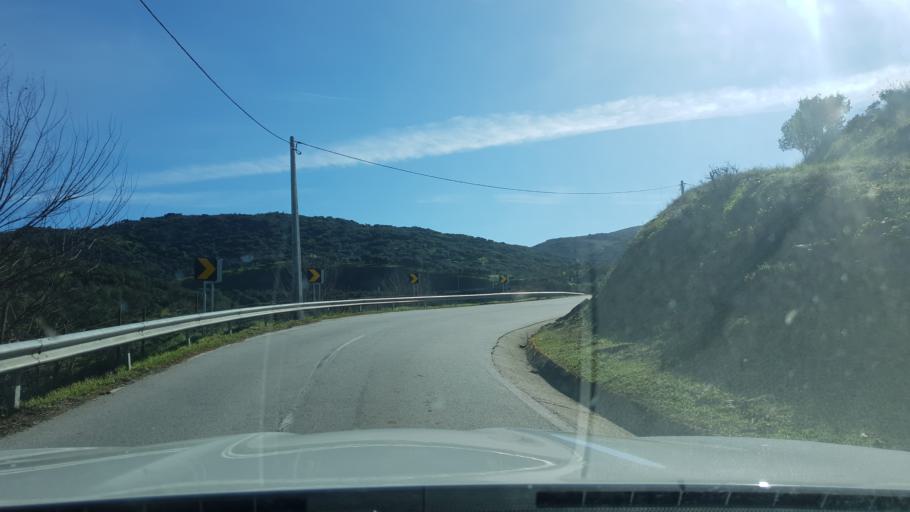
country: PT
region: Braganca
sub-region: Torre de Moncorvo
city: Torre de Moncorvo
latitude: 41.1826
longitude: -7.1019
